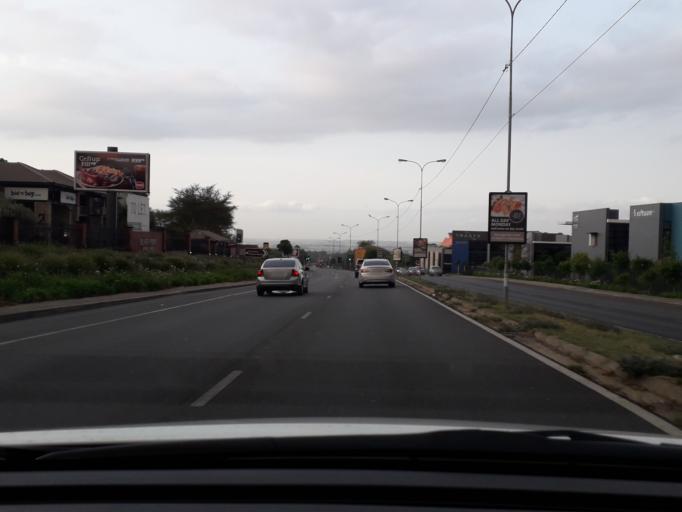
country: ZA
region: Gauteng
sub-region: City of Johannesburg Metropolitan Municipality
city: Diepsloot
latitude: -26.0459
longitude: 28.0249
